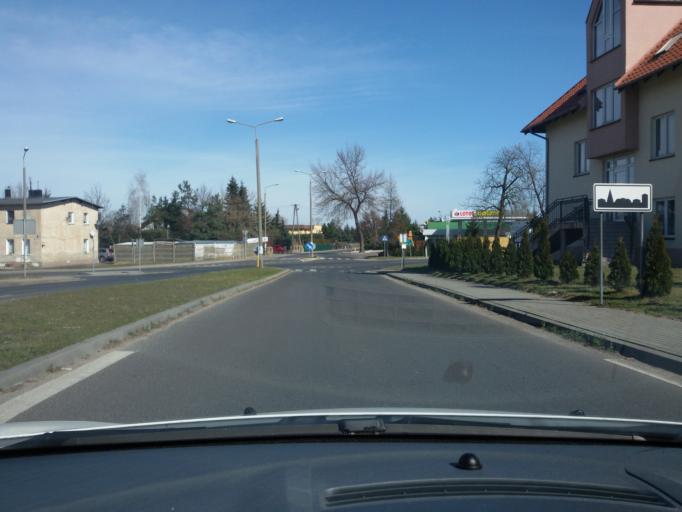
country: PL
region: Greater Poland Voivodeship
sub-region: Powiat leszczynski
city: Rydzyna
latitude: 51.7800
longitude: 16.6709
